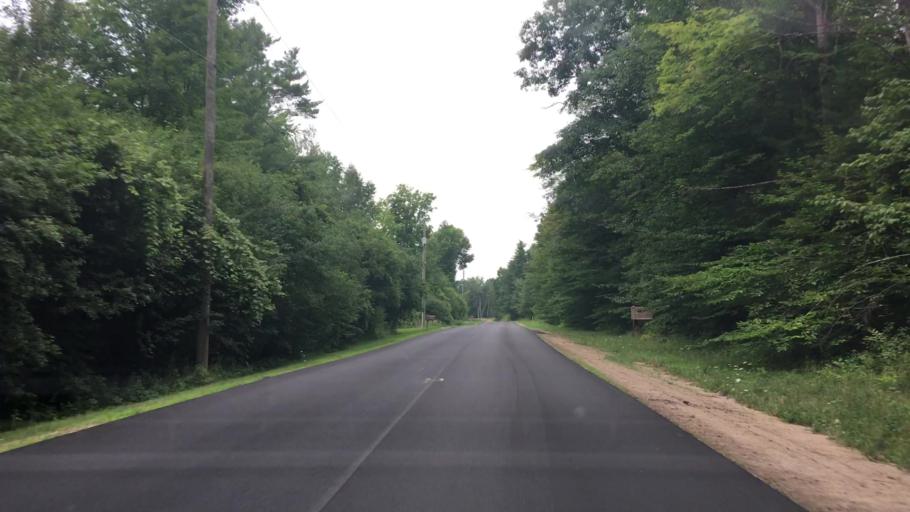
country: US
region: New York
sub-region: Clinton County
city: Peru
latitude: 44.5553
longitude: -73.5660
